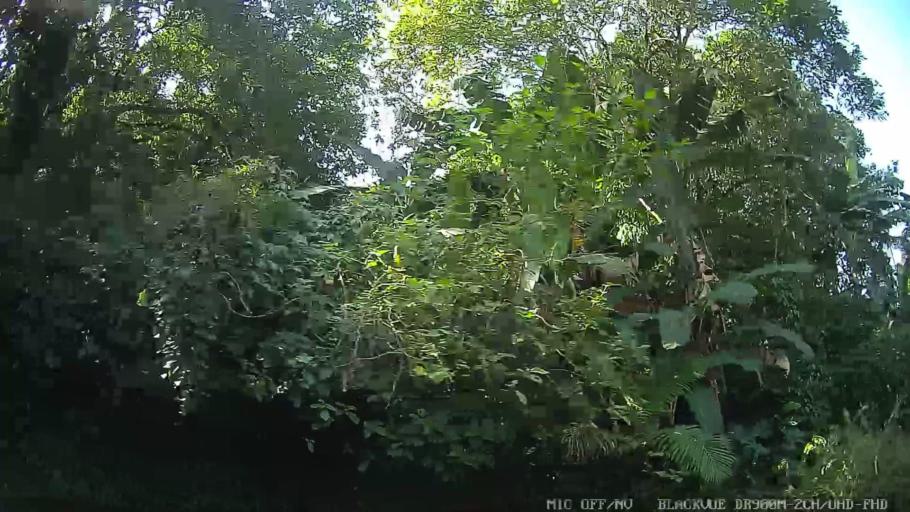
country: BR
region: Sao Paulo
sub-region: Guaruja
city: Guaruja
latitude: -24.0043
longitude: -46.2720
